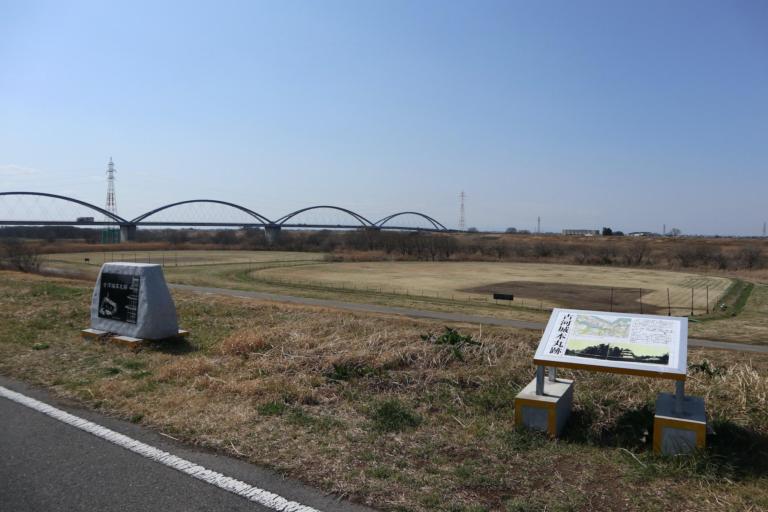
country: JP
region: Ibaraki
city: Koga
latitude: 36.1870
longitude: 139.6962
